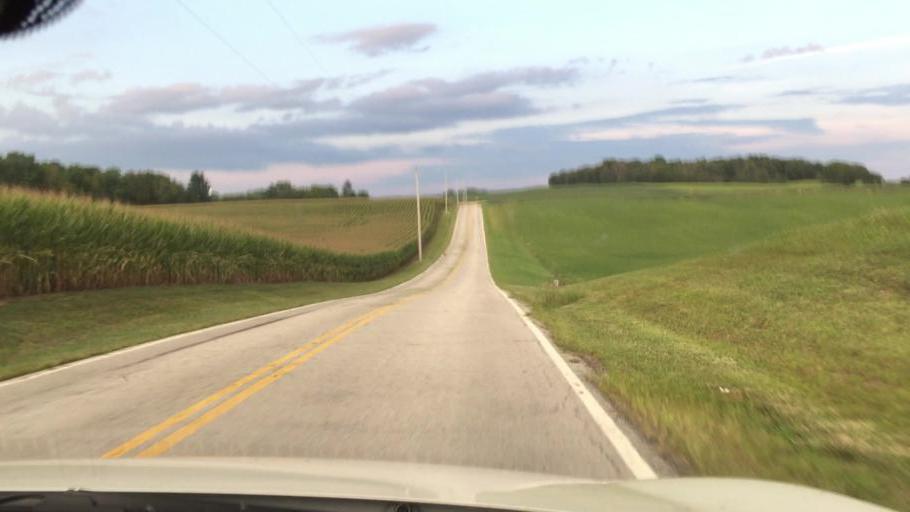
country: US
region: Ohio
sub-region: Champaign County
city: Mechanicsburg
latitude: 39.9951
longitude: -83.6441
